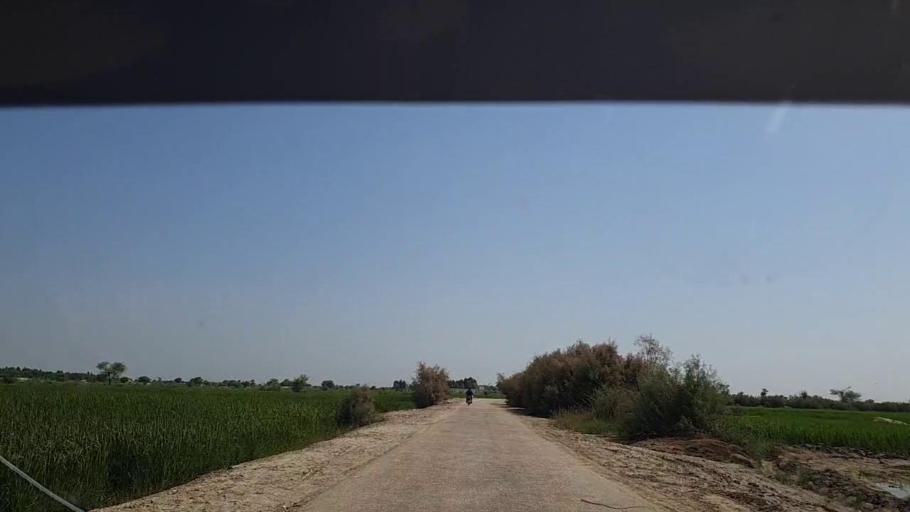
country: PK
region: Sindh
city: Kandhkot
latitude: 28.1694
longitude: 69.1605
